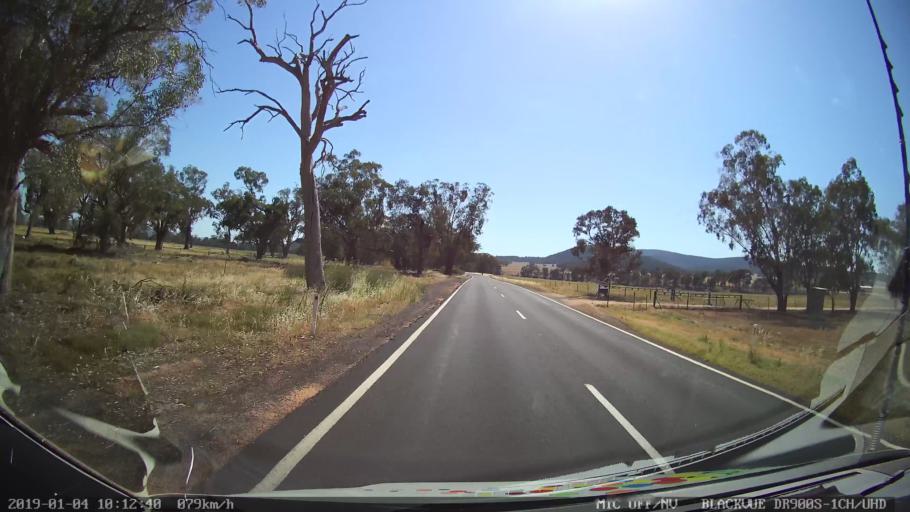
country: AU
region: New South Wales
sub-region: Cabonne
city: Canowindra
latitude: -33.4117
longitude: 148.3977
